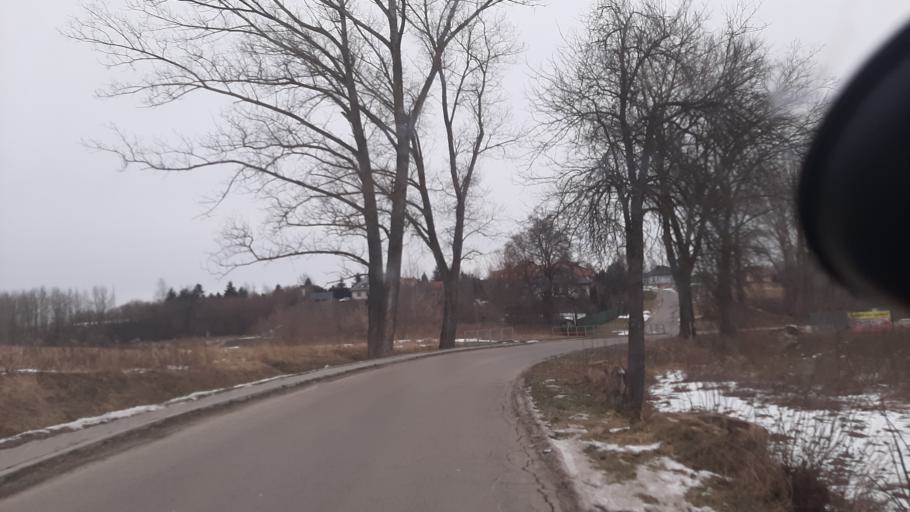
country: PL
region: Lublin Voivodeship
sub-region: Powiat lubelski
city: Jakubowice Murowane
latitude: 51.2817
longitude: 22.6047
